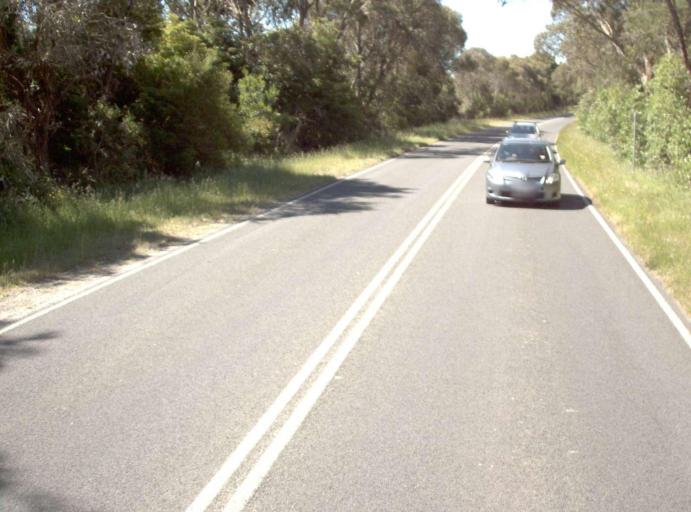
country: AU
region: Victoria
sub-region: Bass Coast
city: North Wonthaggi
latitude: -38.7506
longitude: 146.1352
